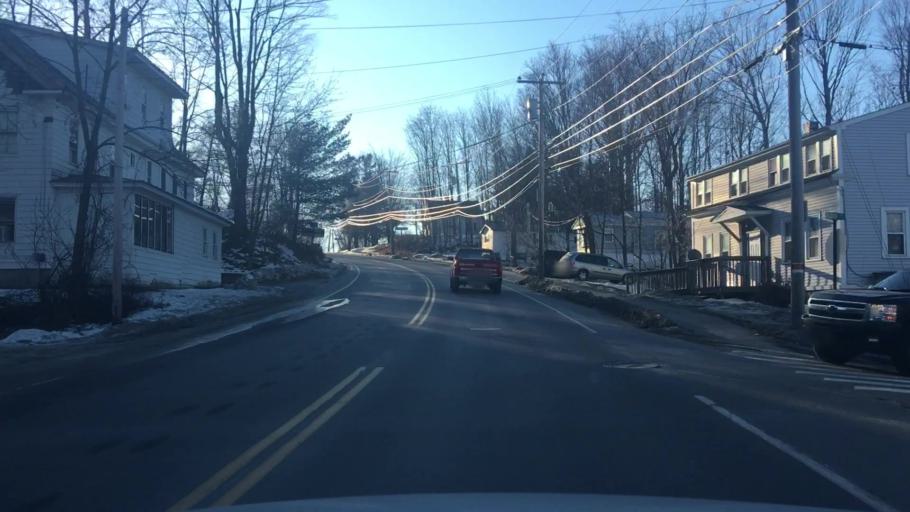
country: US
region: Maine
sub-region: Somerset County
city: Skowhegan
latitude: 44.7615
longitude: -69.7199
